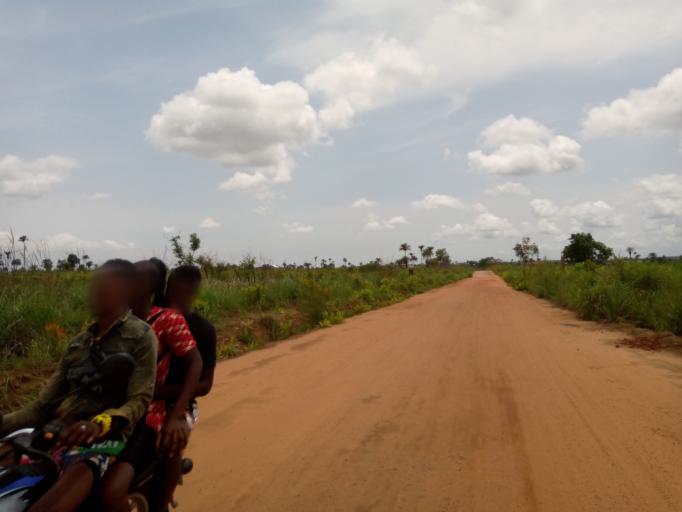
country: SL
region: Western Area
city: Waterloo
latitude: 8.3400
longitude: -12.9450
